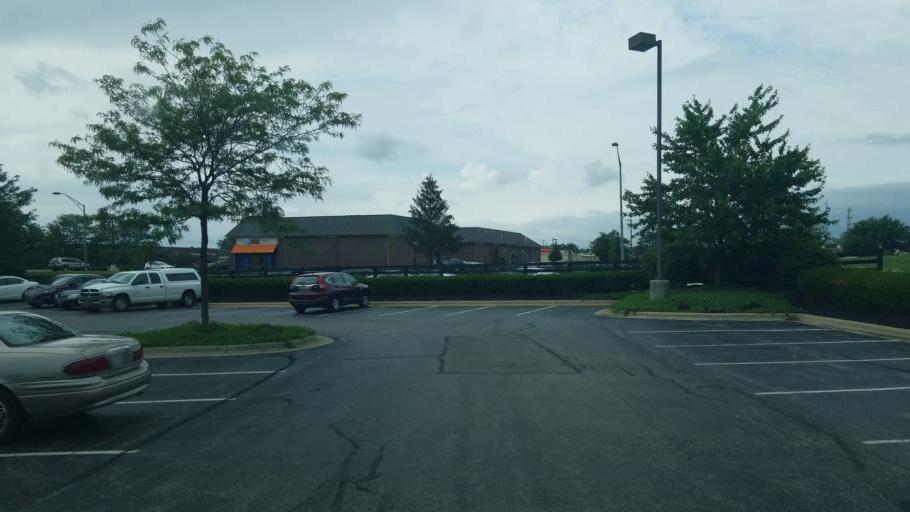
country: US
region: Ohio
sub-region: Franklin County
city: Gahanna
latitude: 40.0577
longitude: -82.8620
